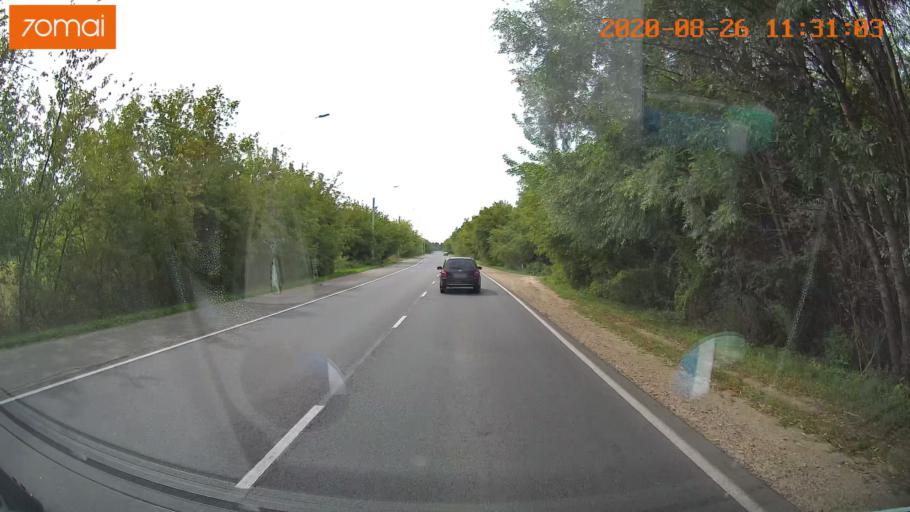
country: RU
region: Rjazan
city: Shilovo
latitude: 54.3102
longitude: 40.8768
